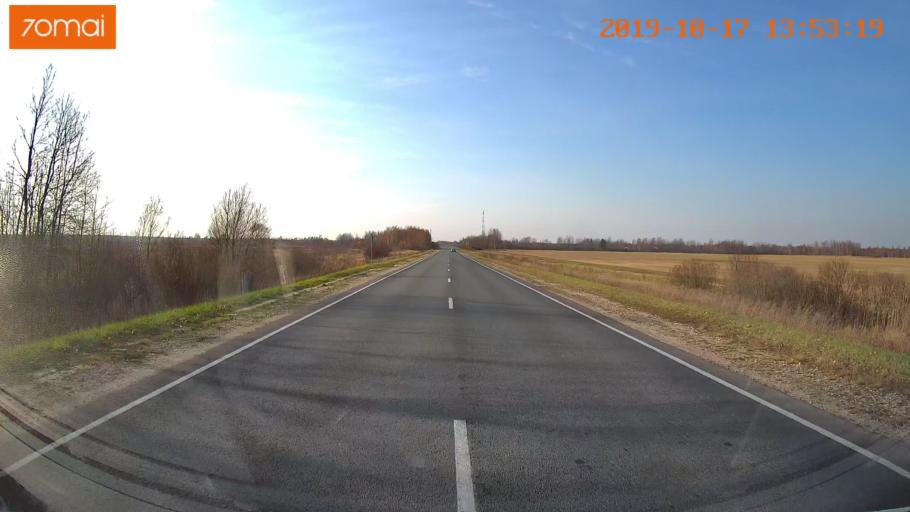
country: RU
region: Rjazan
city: Spas-Klepiki
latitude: 55.1420
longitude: 40.3448
